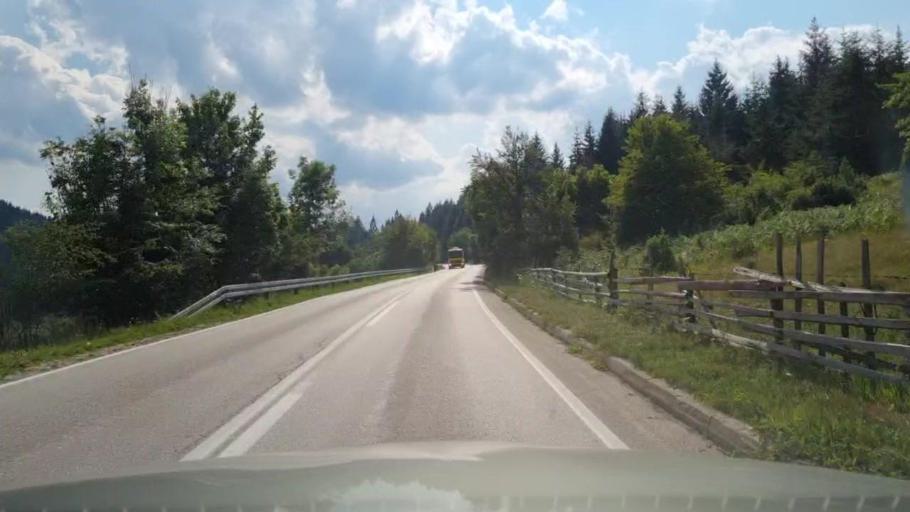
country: BA
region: Federation of Bosnia and Herzegovina
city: Olovo
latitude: 44.0887
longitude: 18.5494
